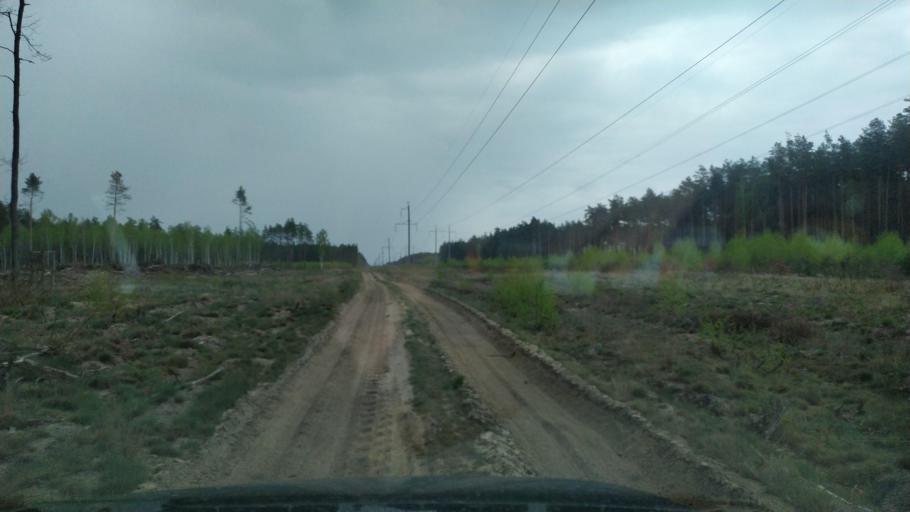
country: BY
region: Brest
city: Pruzhany
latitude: 52.3603
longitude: 24.5903
